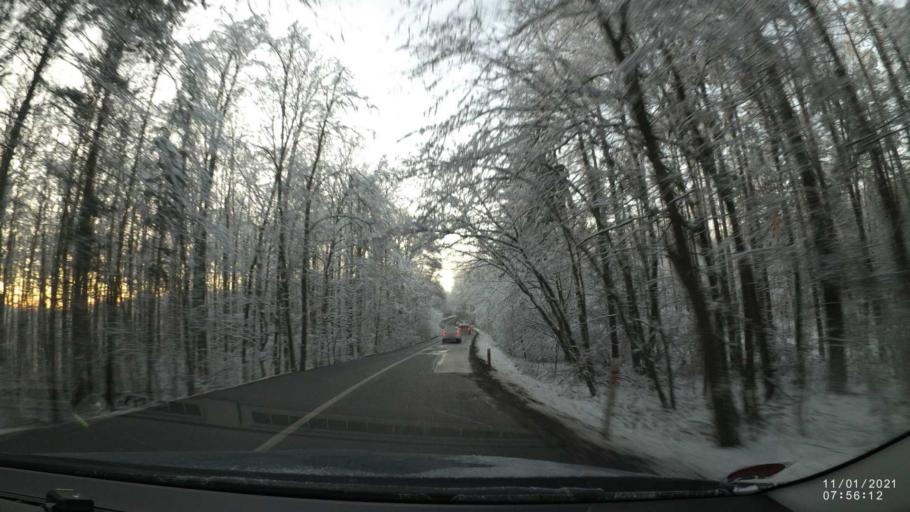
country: CZ
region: South Moravian
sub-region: Okres Blansko
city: Adamov
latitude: 49.2758
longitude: 16.6306
